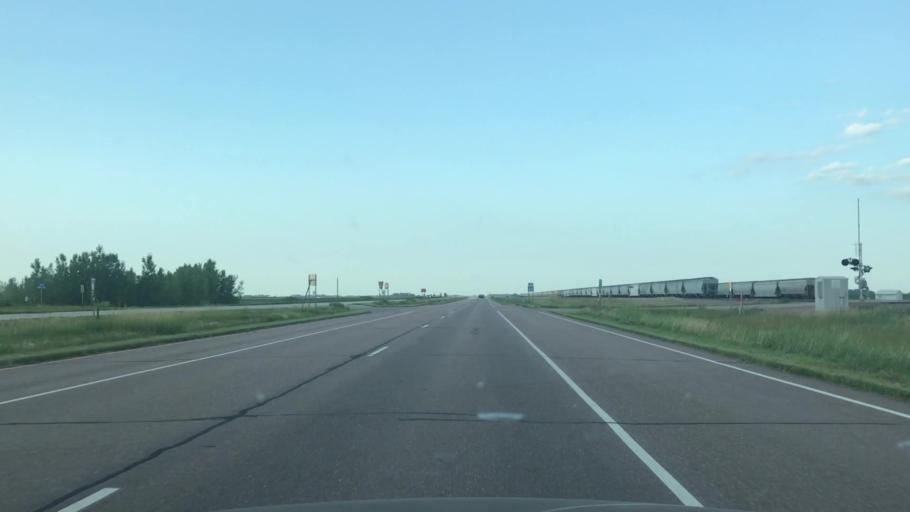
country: US
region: Minnesota
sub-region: Nobles County
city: Worthington
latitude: 43.7210
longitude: -95.4370
